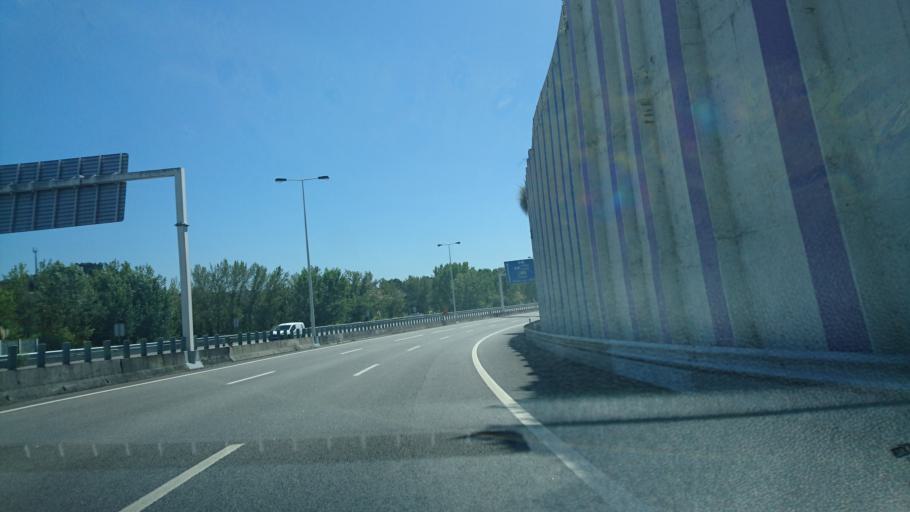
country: PT
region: Porto
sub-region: Gondomar
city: Valbom
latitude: 41.1548
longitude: -8.5725
